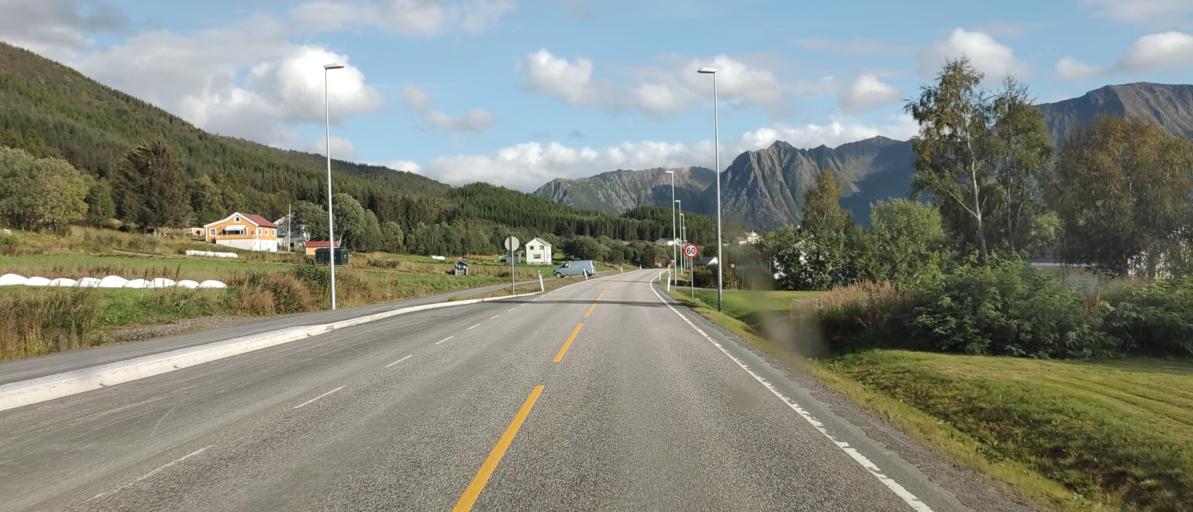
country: NO
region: Nordland
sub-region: Sortland
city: Sortland
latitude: 68.7496
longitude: 15.4952
